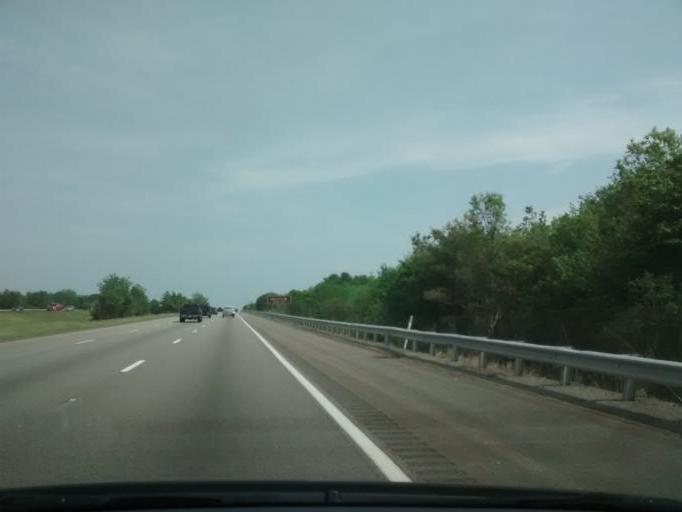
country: US
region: Massachusetts
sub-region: Bristol County
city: Mansfield Center
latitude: 42.0149
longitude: -71.2371
